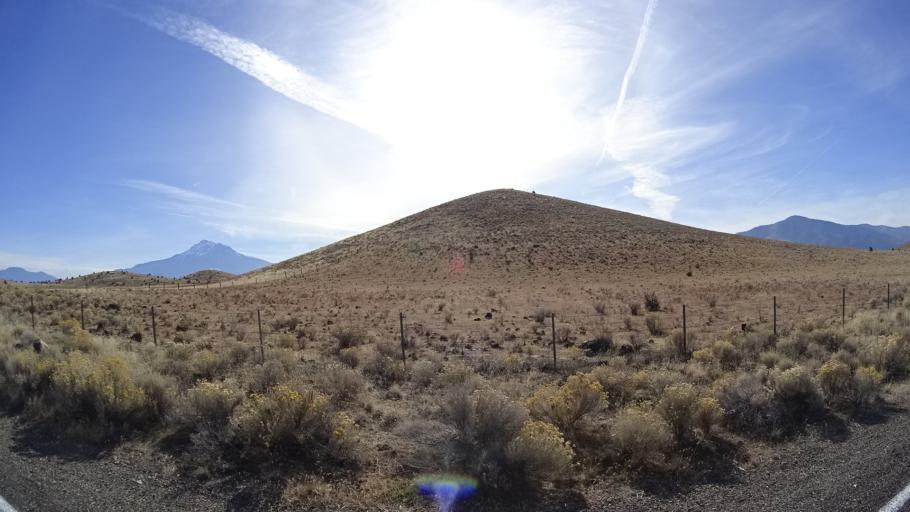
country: US
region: California
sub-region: Siskiyou County
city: Weed
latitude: 41.5514
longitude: -122.4878
